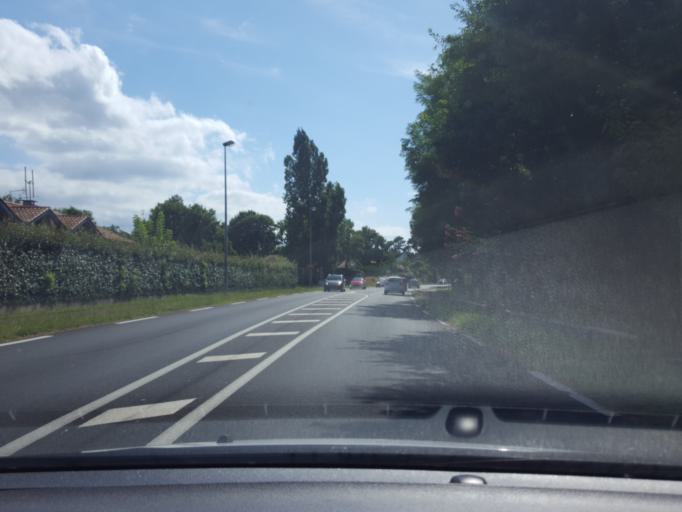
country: FR
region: Aquitaine
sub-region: Departement des Landes
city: Capbreton
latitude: 43.6331
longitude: -1.4277
